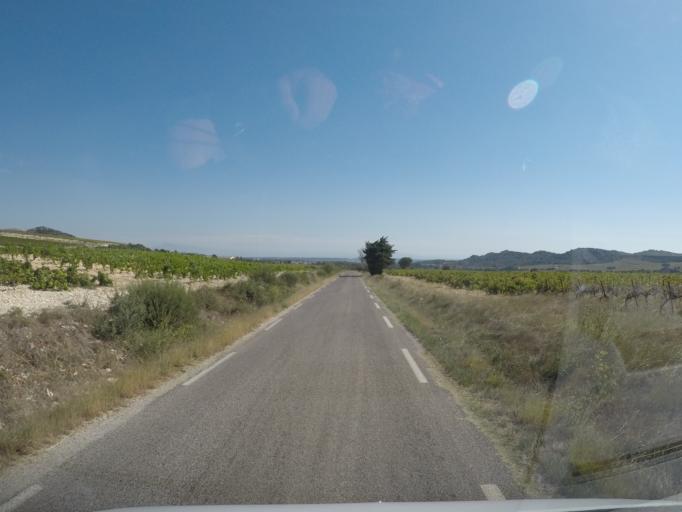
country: FR
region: Languedoc-Roussillon
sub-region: Departement du Gard
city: Tavel
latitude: 44.0115
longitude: 4.6770
